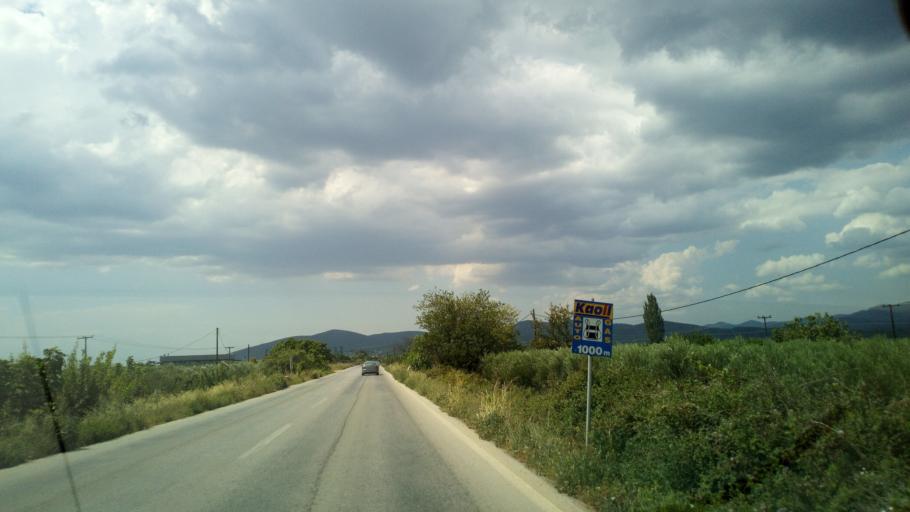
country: GR
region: Central Macedonia
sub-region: Nomos Chalkidikis
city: Ormylia
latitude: 40.2552
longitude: 23.5415
